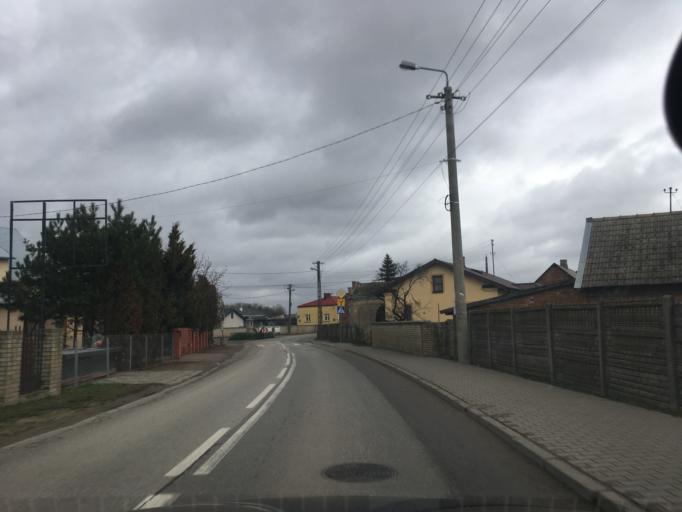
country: PL
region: Masovian Voivodeship
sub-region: Powiat pruszkowski
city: Rybie
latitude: 52.1252
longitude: 20.9547
